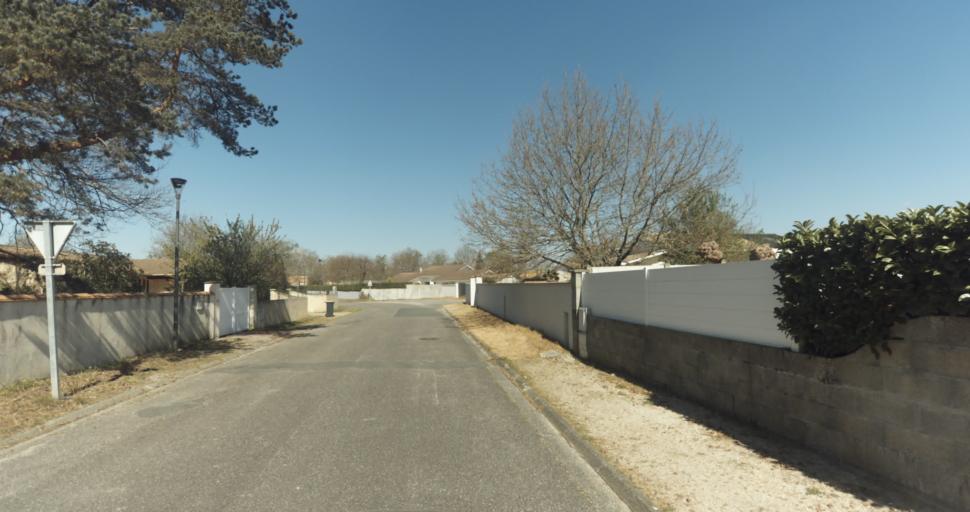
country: FR
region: Aquitaine
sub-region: Departement de la Gironde
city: Martignas-sur-Jalle
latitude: 44.7999
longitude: -0.7910
